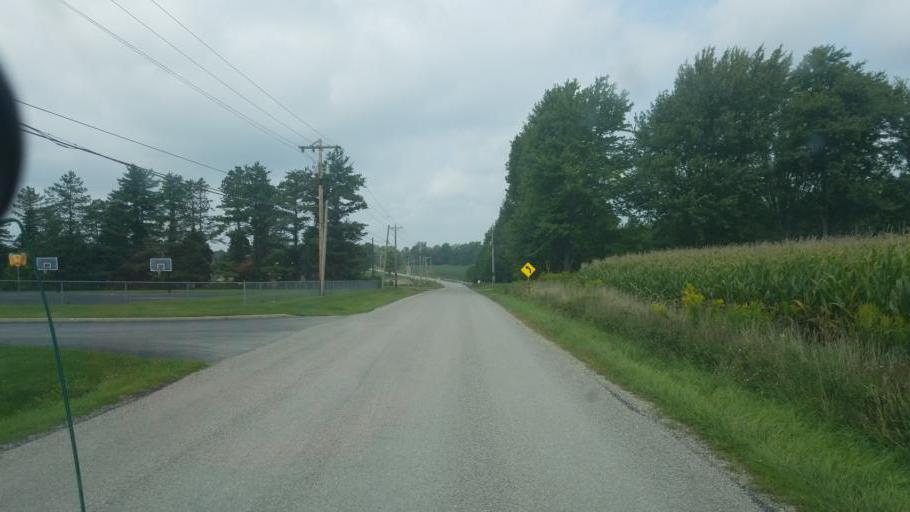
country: US
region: Ohio
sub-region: Huron County
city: Greenwich
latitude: 41.0490
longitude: -82.5183
